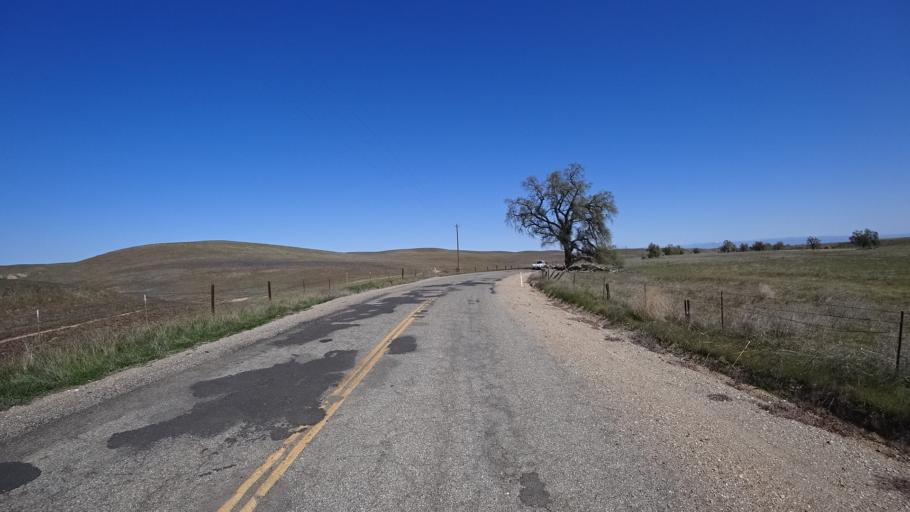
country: US
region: California
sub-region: Glenn County
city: Orland
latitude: 39.7732
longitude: -122.3219
